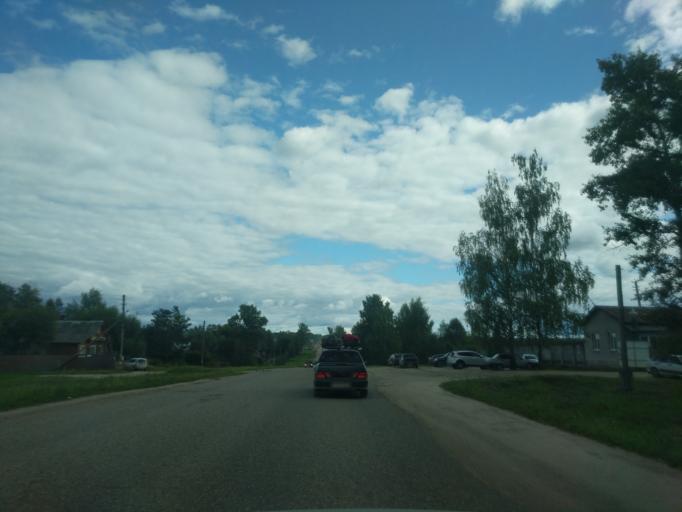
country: RU
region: Kostroma
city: Sudislavl'
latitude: 57.8803
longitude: 41.7201
